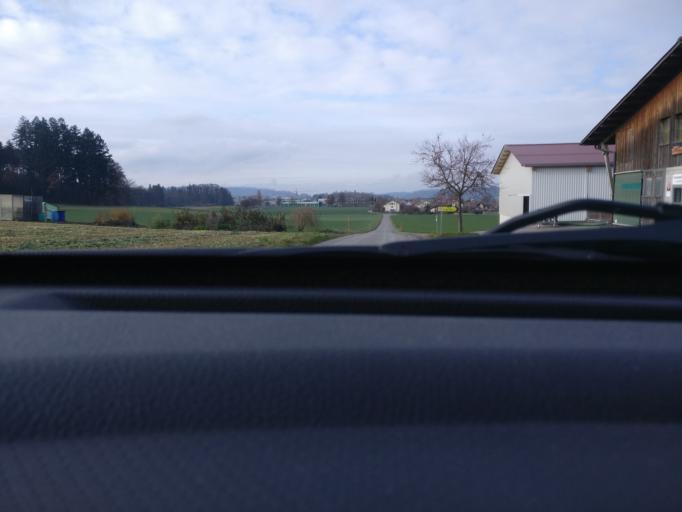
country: CH
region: Bern
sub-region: Bern-Mittelland District
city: Urtenen
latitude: 47.0083
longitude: 7.4881
